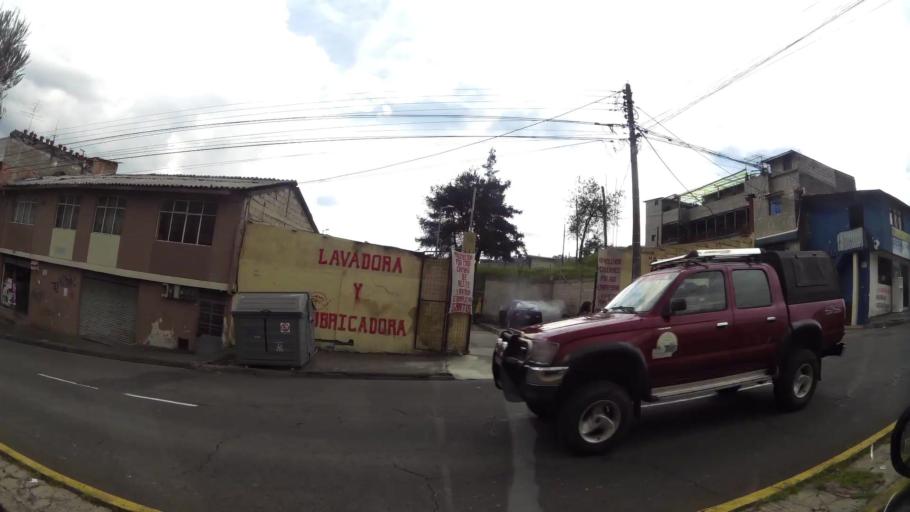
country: EC
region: Pichincha
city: Quito
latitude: -0.2438
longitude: -78.5116
